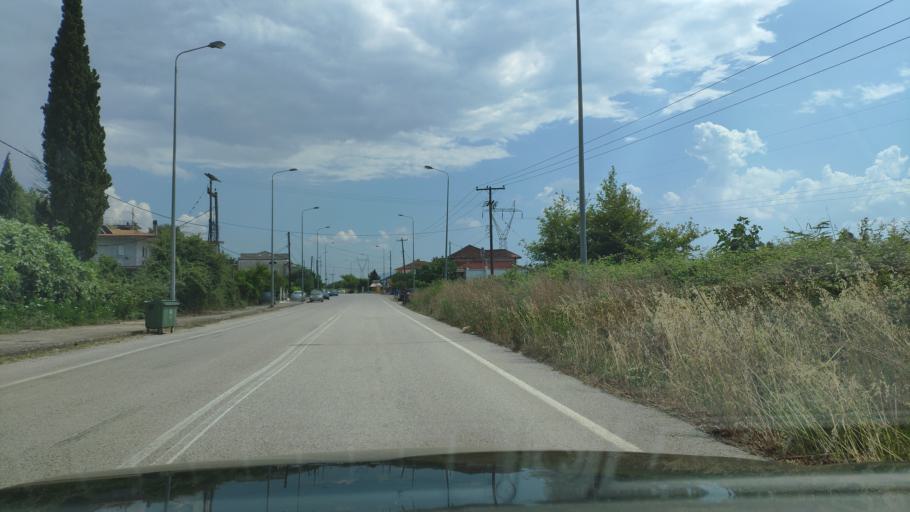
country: GR
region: West Greece
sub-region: Nomos Aitolias kai Akarnanias
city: Krikellos
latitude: 38.9730
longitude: 21.1676
